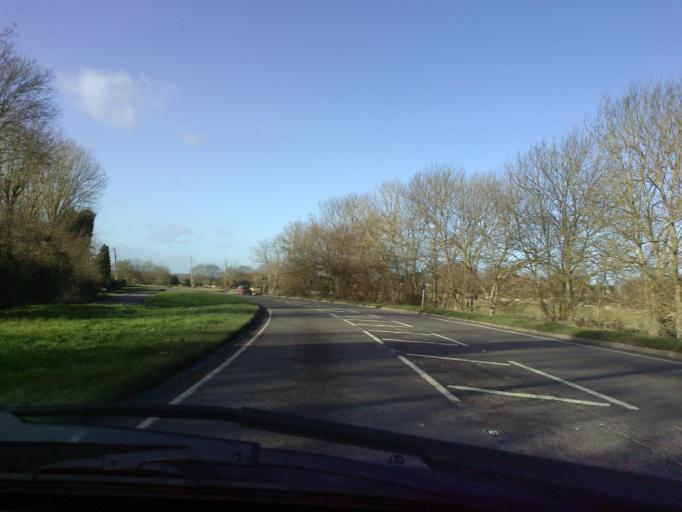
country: GB
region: England
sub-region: Hampshire
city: Romsey
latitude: 51.0258
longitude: -1.5097
